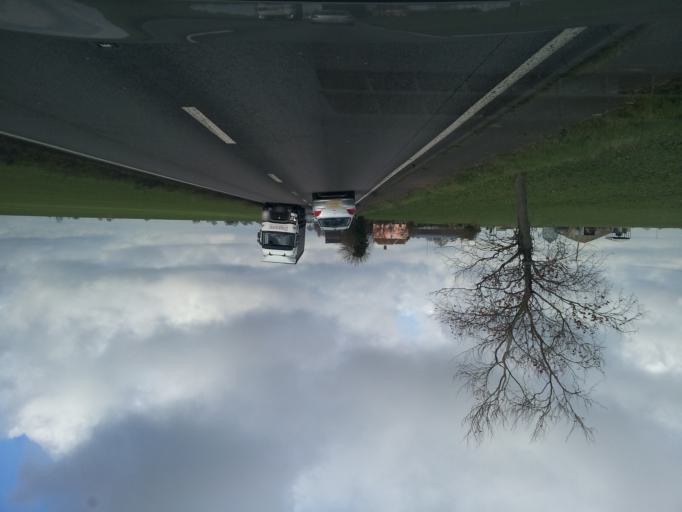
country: GB
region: England
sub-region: Suffolk
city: Needham Market
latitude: 52.2048
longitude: 1.1010
